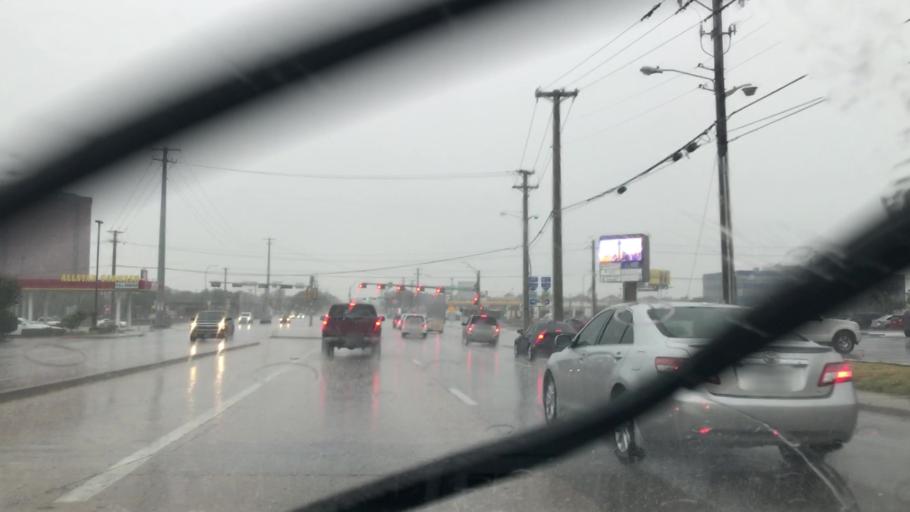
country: US
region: Texas
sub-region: Dallas County
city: Addison
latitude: 32.9273
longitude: -96.8036
